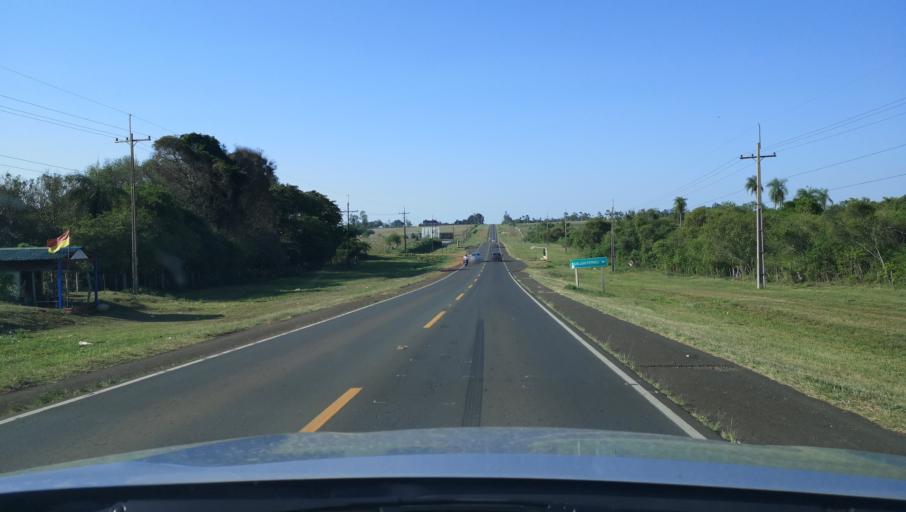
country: PY
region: Misiones
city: Santa Maria
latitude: -26.8344
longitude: -57.0330
